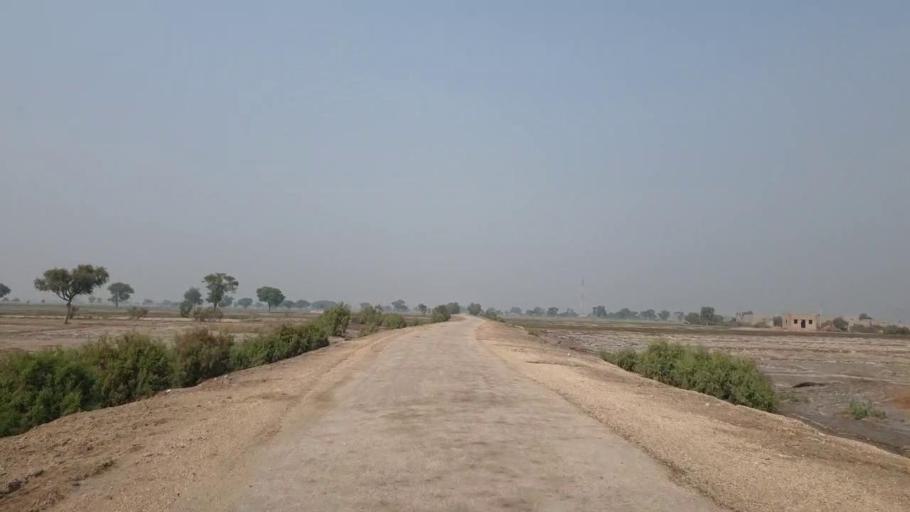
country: PK
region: Sindh
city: Bhan
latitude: 26.4913
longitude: 67.7004
